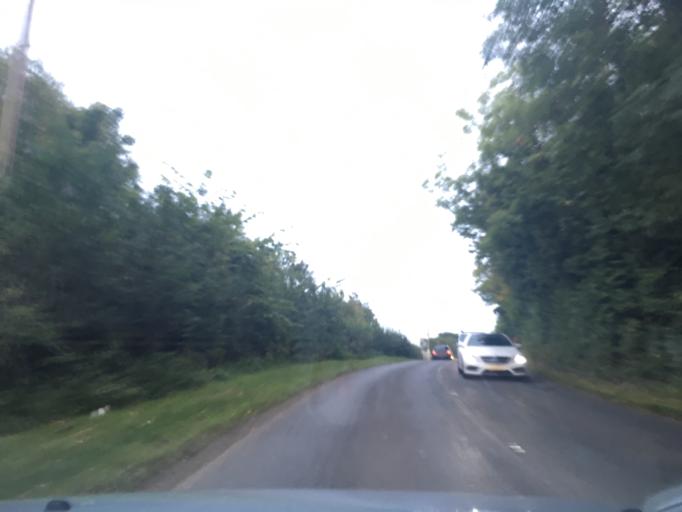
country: GB
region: England
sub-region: Oxfordshire
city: Kidlington
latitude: 51.8204
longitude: -1.2348
